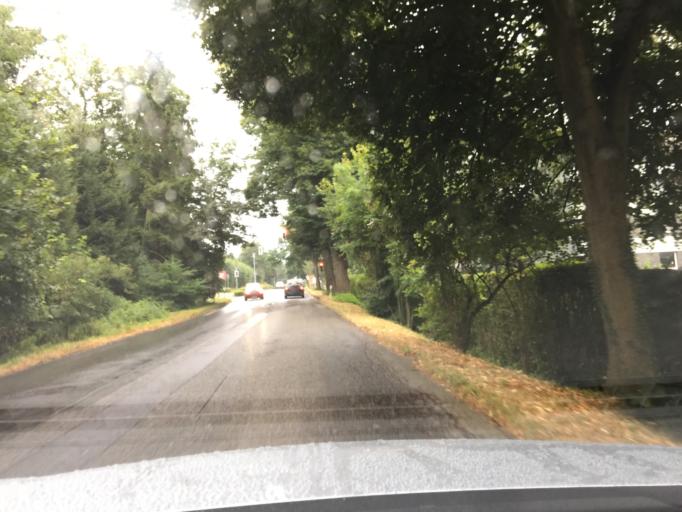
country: DE
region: North Rhine-Westphalia
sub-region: Regierungsbezirk Dusseldorf
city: Ratingen
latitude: 51.3379
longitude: 6.8986
